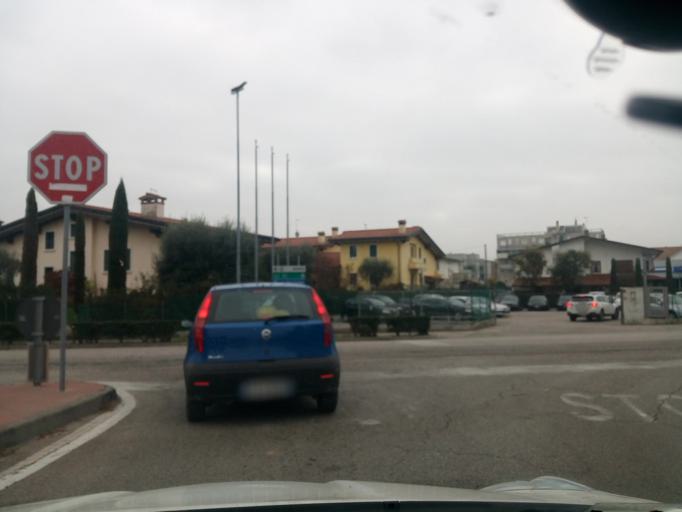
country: IT
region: Veneto
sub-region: Provincia di Vicenza
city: Sandrigo
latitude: 45.6635
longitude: 11.5951
